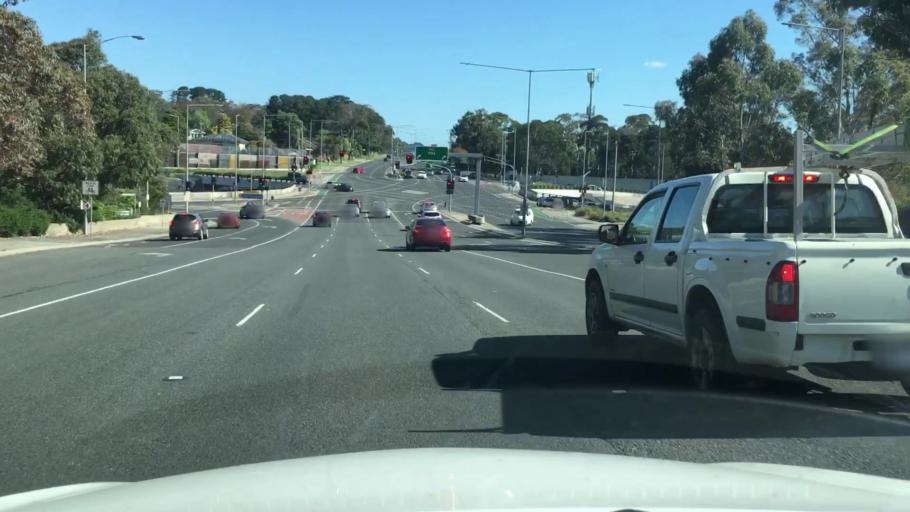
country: AU
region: Victoria
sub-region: Manningham
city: Donvale
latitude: -37.8025
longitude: 145.1781
